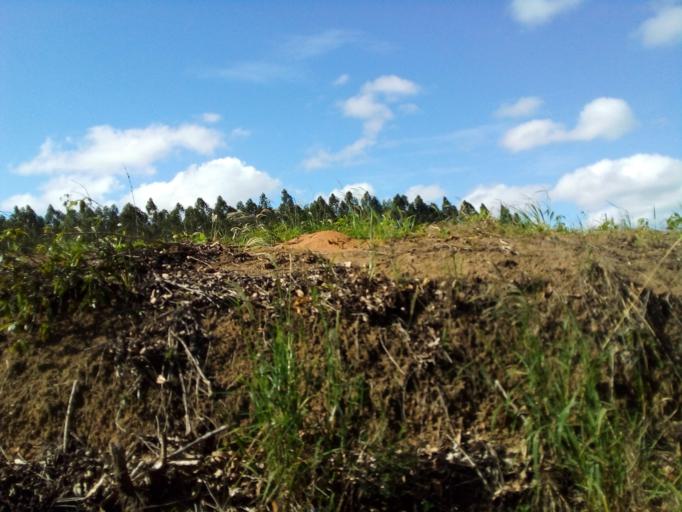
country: BR
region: Espirito Santo
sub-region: Aracruz
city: Aracruz
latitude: -19.7126
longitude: -40.2116
